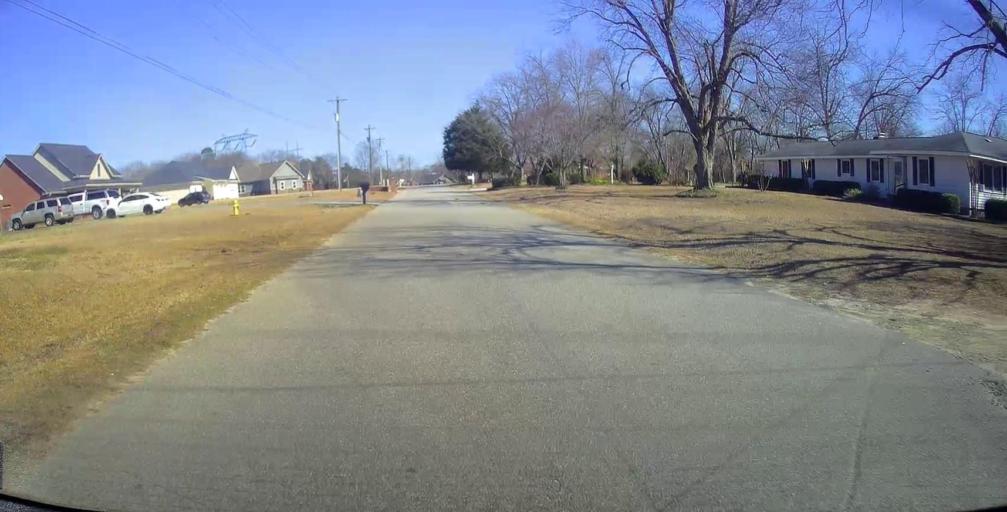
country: US
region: Georgia
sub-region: Peach County
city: Byron
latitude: 32.6356
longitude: -83.7598
